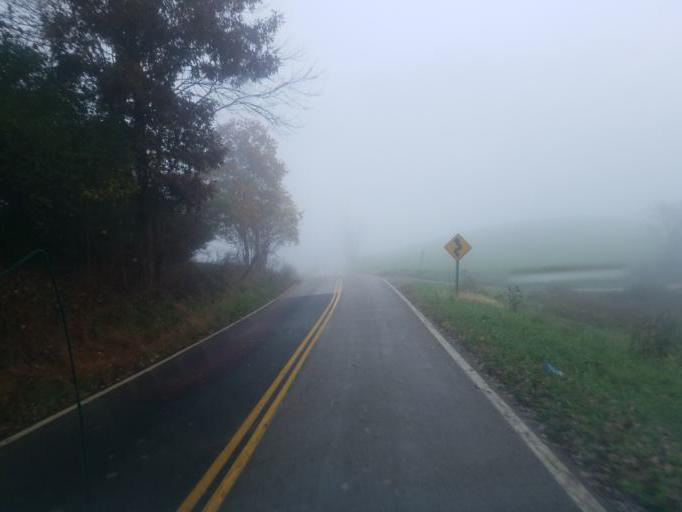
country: US
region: Ohio
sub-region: Morgan County
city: McConnelsville
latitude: 39.5174
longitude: -81.9291
